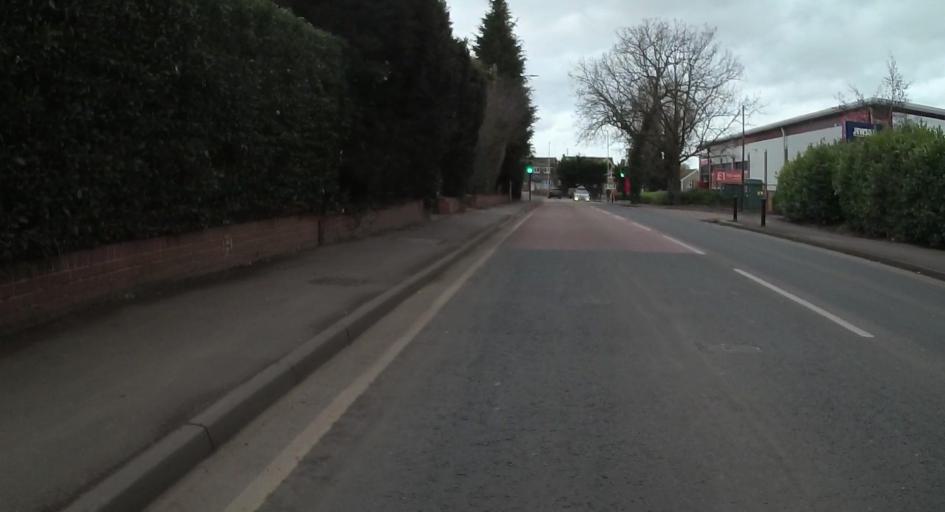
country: GB
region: England
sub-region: Wokingham
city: Wokingham
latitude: 51.4072
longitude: -0.8480
